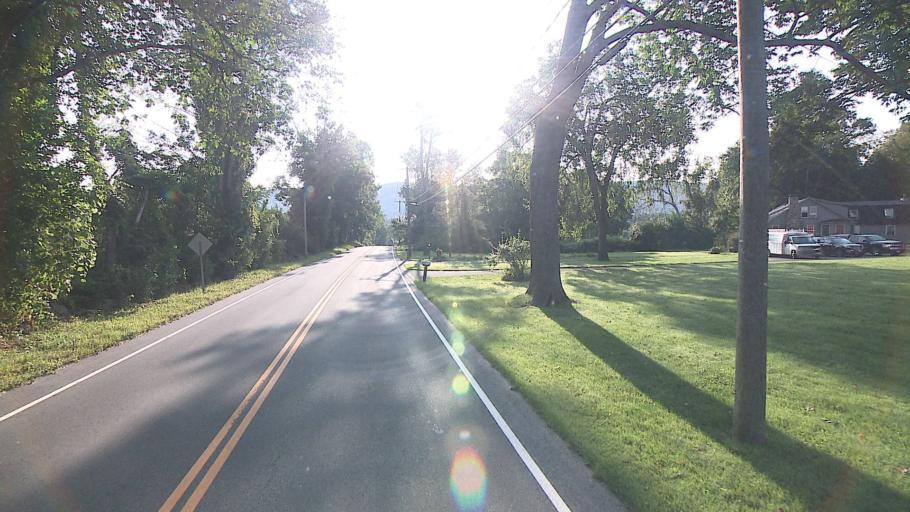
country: US
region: Connecticut
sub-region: Litchfield County
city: Kent
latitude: 41.7401
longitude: -73.4612
